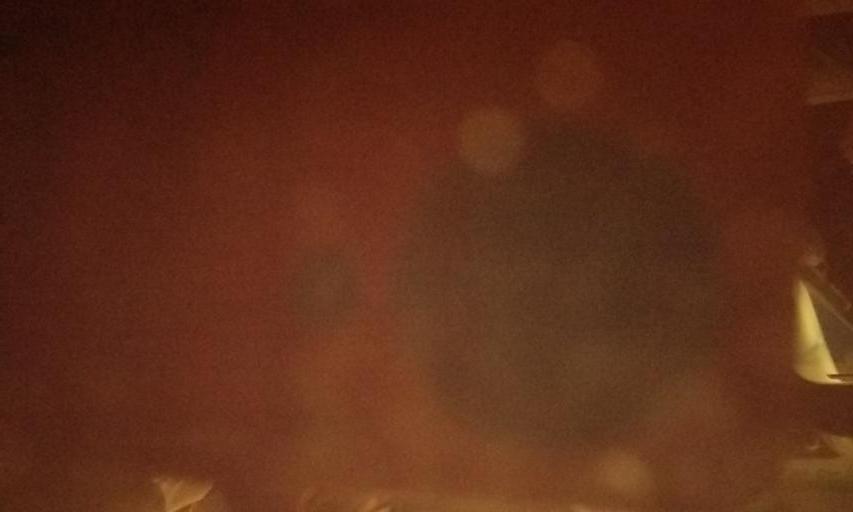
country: JP
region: Hyogo
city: Kobe
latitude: 34.7167
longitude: 135.2230
